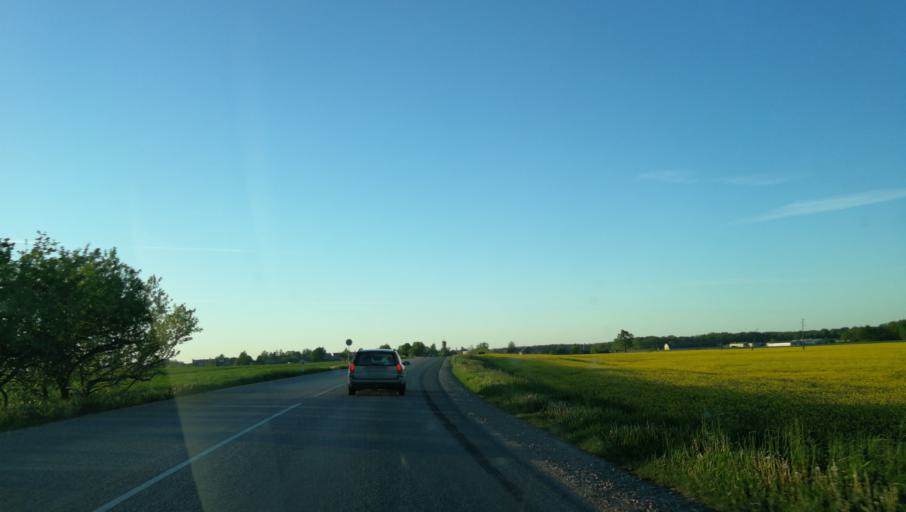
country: LV
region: Dobeles Rajons
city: Dobele
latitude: 56.7279
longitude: 23.3896
